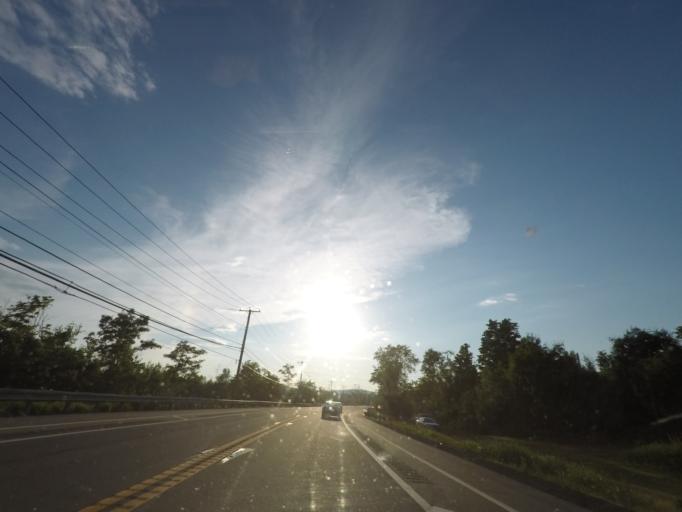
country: US
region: Massachusetts
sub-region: Hampden County
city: Brimfield
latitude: 42.1103
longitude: -72.1789
